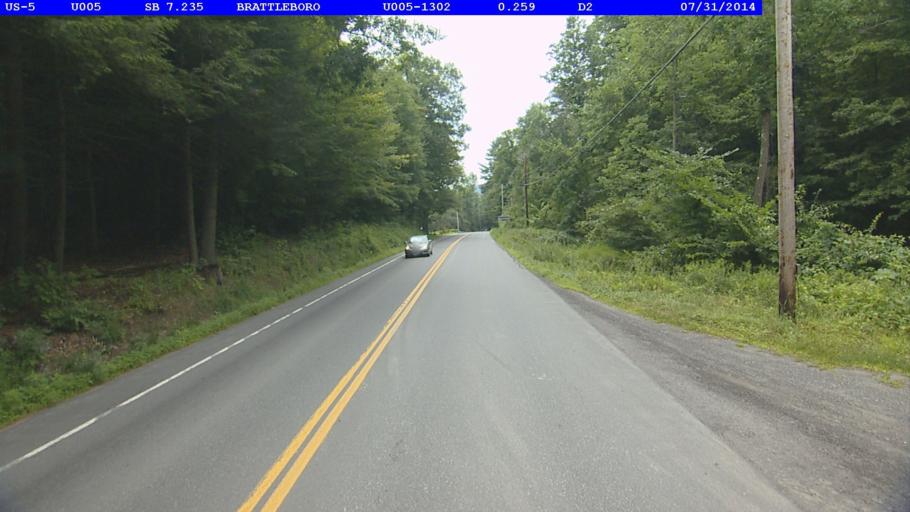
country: US
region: Vermont
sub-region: Windham County
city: Brattleboro
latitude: 42.8282
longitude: -72.5737
